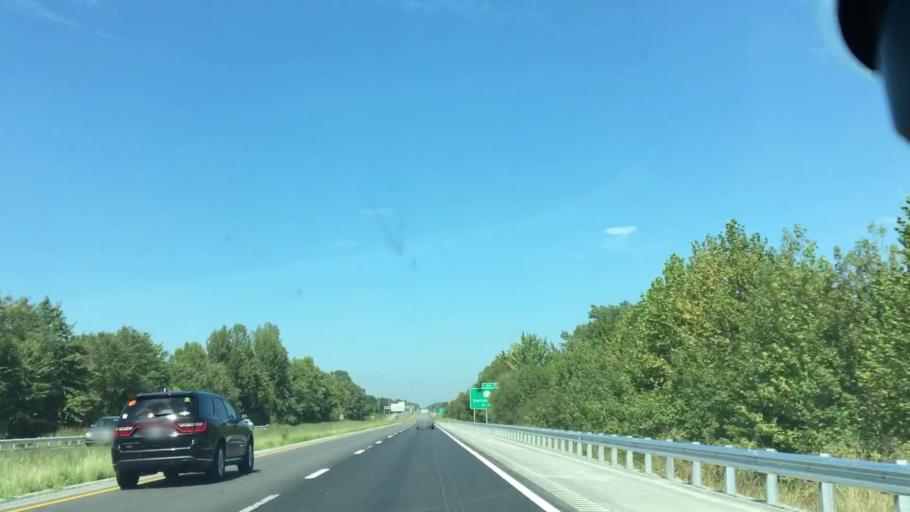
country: US
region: Kentucky
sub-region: Hopkins County
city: Nortonville
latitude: 37.2406
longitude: -87.4475
